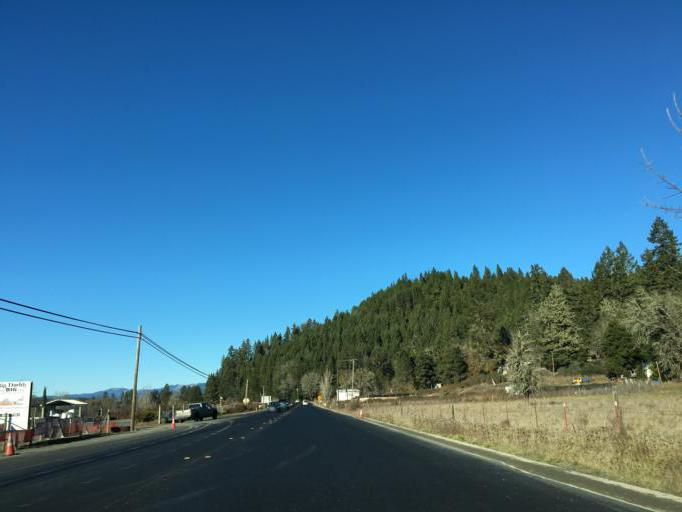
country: US
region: California
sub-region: Mendocino County
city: Laytonville
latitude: 39.6528
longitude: -123.4764
